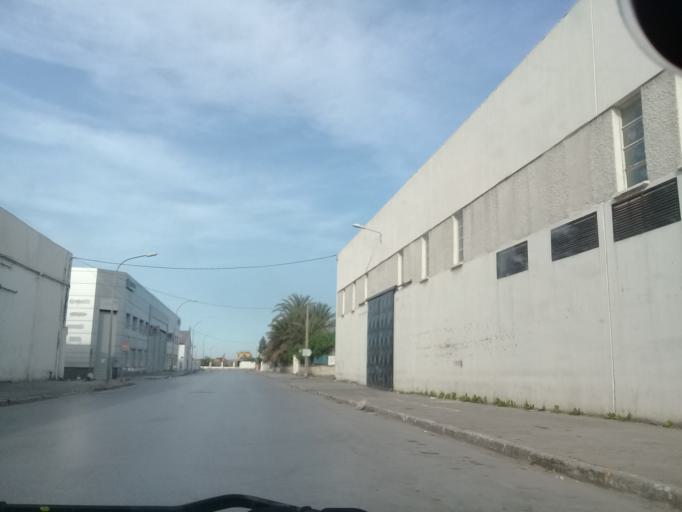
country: TN
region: Tunis
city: Tunis
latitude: 36.7903
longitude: 10.1854
